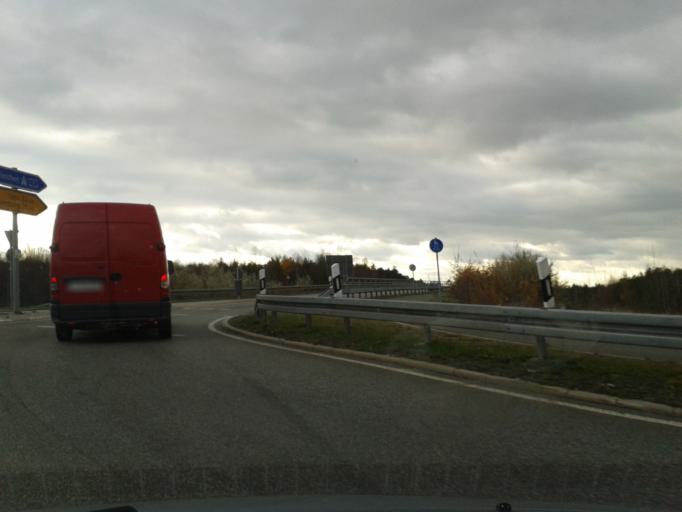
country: DE
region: Thuringia
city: Hermsdorf
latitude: 50.9121
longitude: 11.8434
